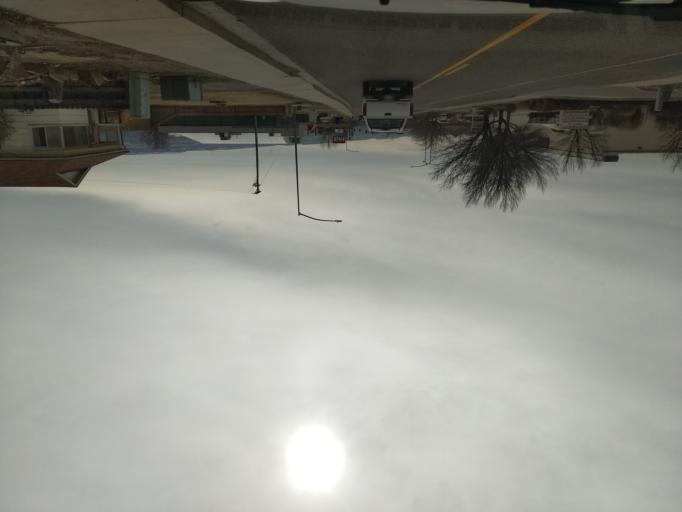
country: US
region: Colorado
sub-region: Mesa County
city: Grand Junction
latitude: 39.0799
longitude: -108.5292
